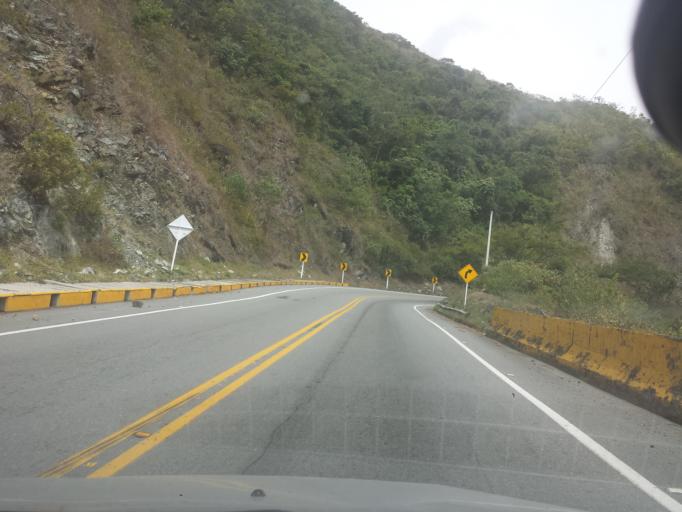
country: CO
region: Antioquia
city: Antioquia
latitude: 6.6119
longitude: -75.8499
